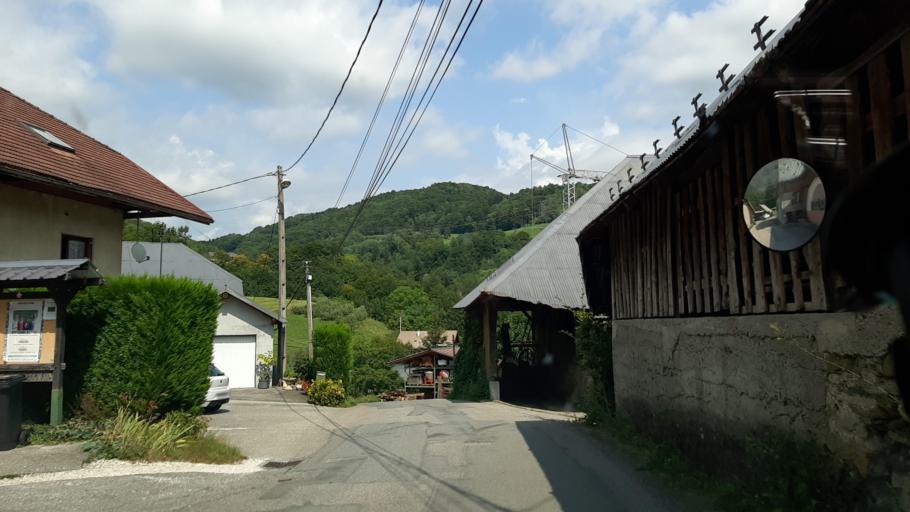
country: FR
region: Rhone-Alpes
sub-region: Departement de la Savoie
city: Mercury
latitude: 45.6866
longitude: 6.3596
